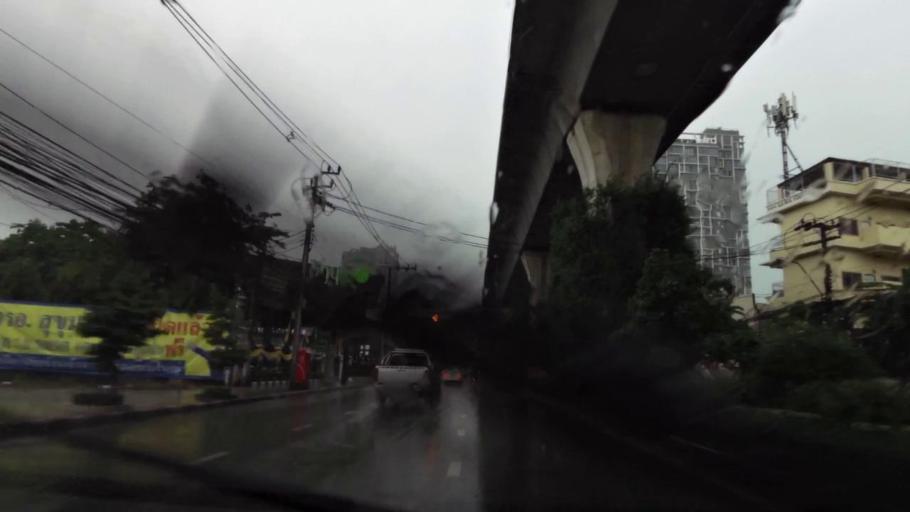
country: TH
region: Bangkok
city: Phra Khanong
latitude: 13.7024
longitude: 100.6025
